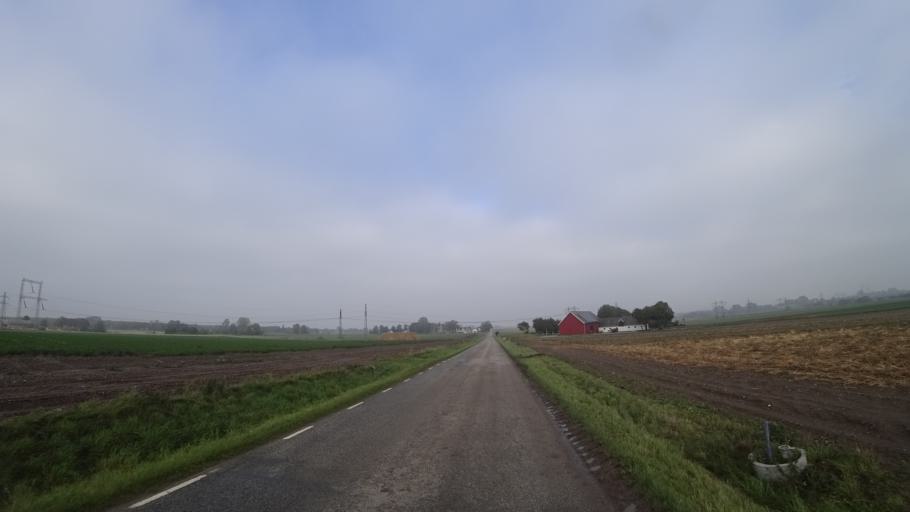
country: SE
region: Skane
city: Bjarred
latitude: 55.7415
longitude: 12.9926
